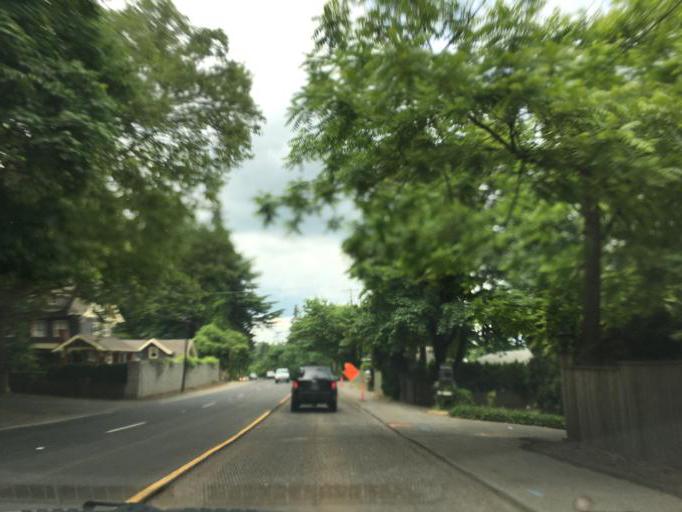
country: US
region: Oregon
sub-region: Clackamas County
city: Milwaukie
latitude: 45.4520
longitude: -122.6597
